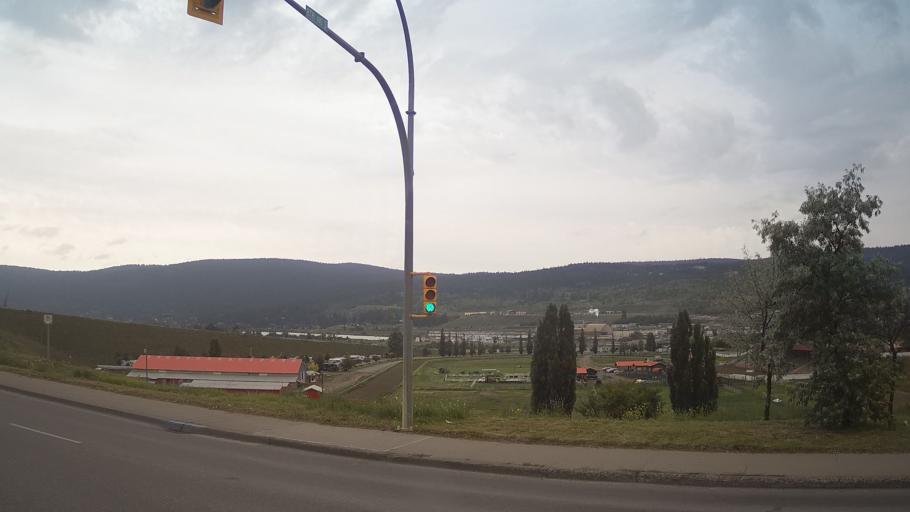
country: CA
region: British Columbia
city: Williams Lake
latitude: 52.1285
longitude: -122.1332
